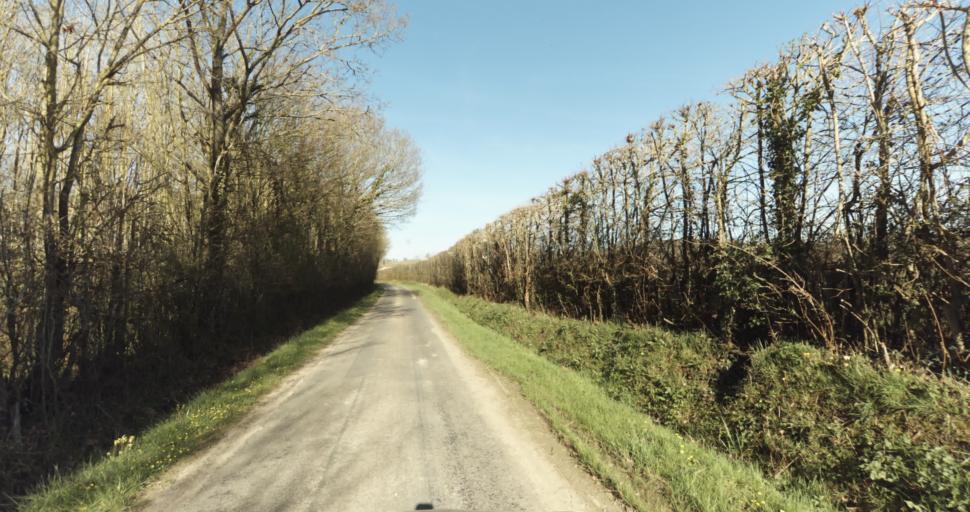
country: FR
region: Lower Normandy
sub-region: Departement du Calvados
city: Livarot
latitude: 49.0457
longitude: 0.0793
